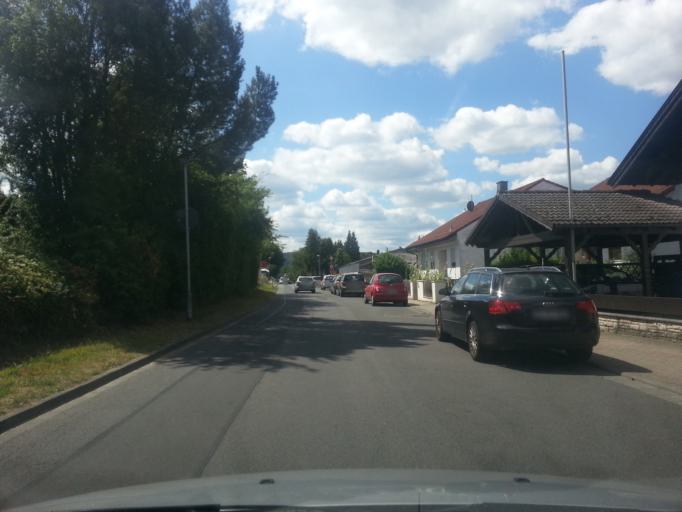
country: DE
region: Hesse
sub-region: Regierungsbezirk Darmstadt
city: Bad Konig
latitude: 49.7399
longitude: 9.0019
